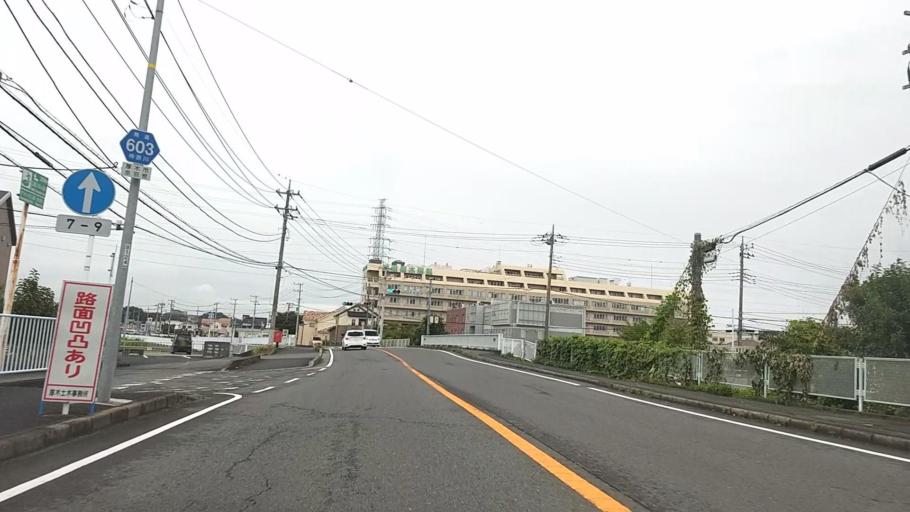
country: JP
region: Kanagawa
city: Atsugi
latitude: 35.4315
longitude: 139.3527
